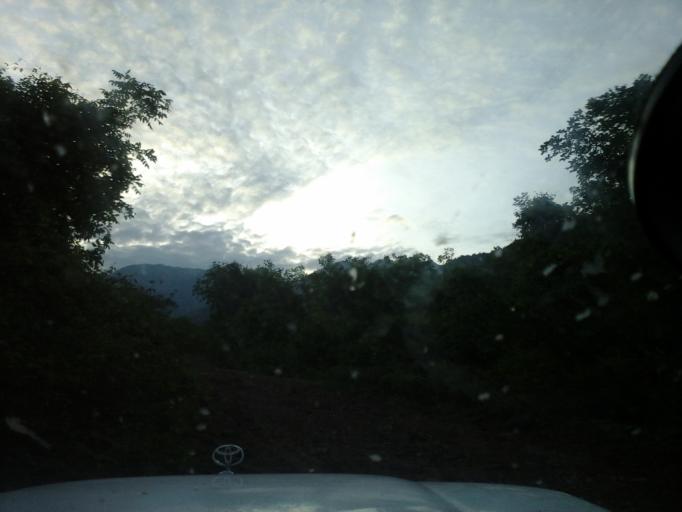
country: CO
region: Cesar
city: Agustin Codazzi
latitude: 10.1727
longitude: -73.1572
